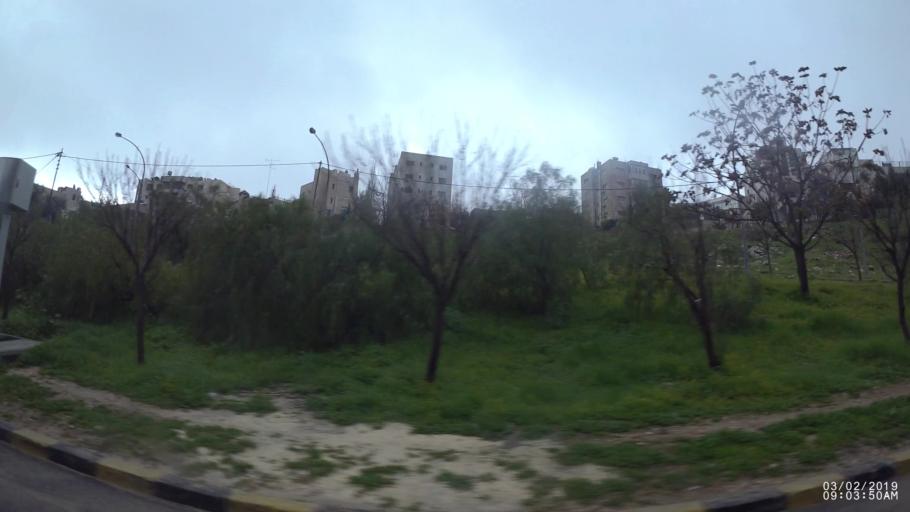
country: JO
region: Amman
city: Amman
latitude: 31.9592
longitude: 35.9009
